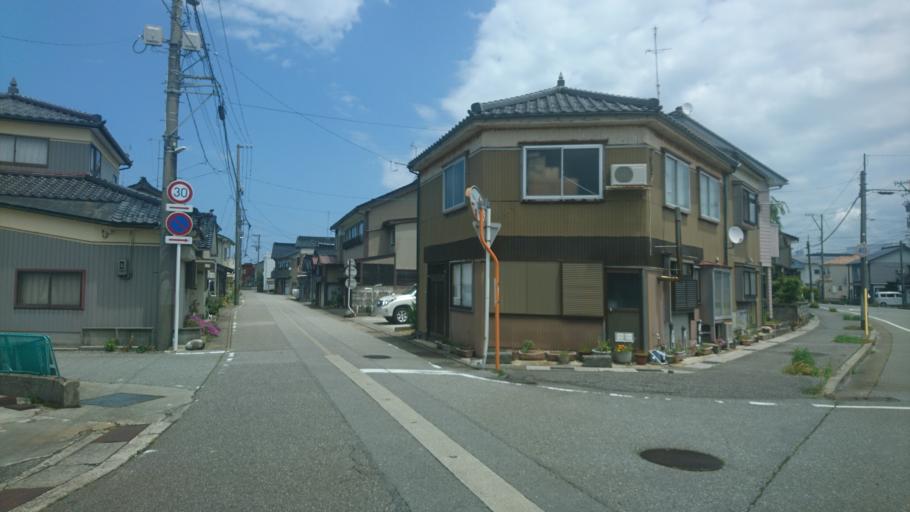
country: JP
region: Toyama
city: Nyuzen
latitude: 36.9336
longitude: 137.4986
